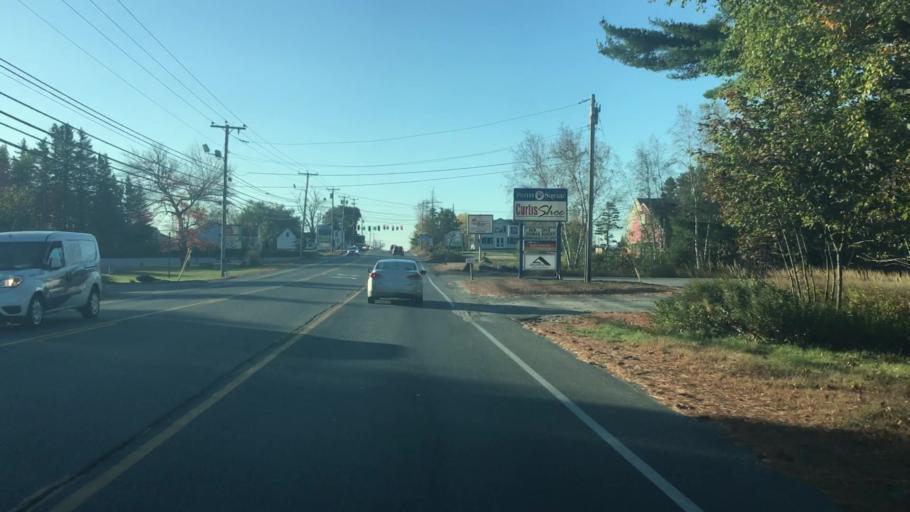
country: US
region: Maine
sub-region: Hancock County
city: Ellsworth
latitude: 44.5214
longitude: -68.3966
